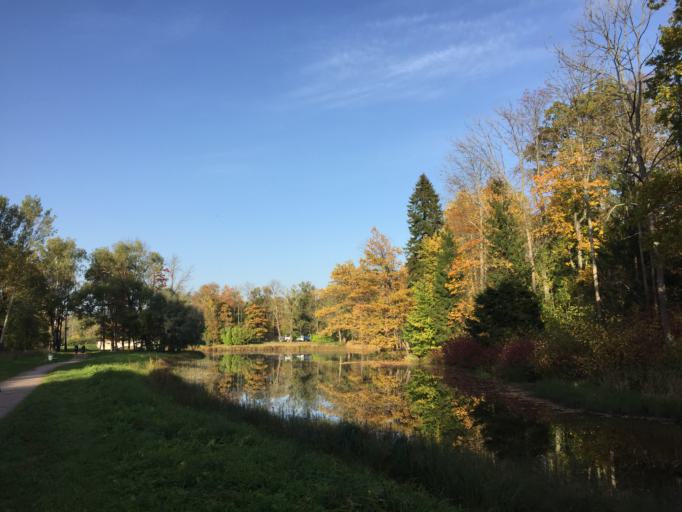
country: RU
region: St.-Petersburg
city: Pushkin
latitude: 59.7204
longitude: 30.3716
